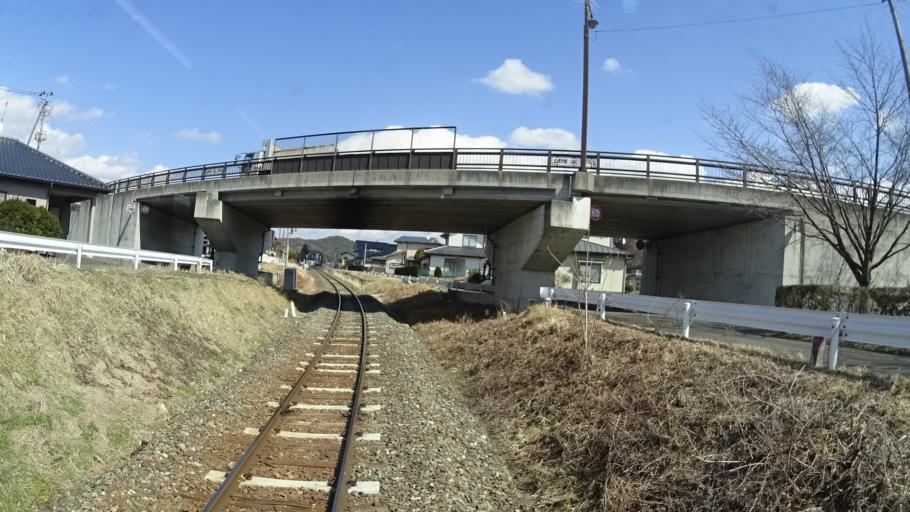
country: JP
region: Iwate
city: Tono
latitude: 39.3315
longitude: 141.5368
